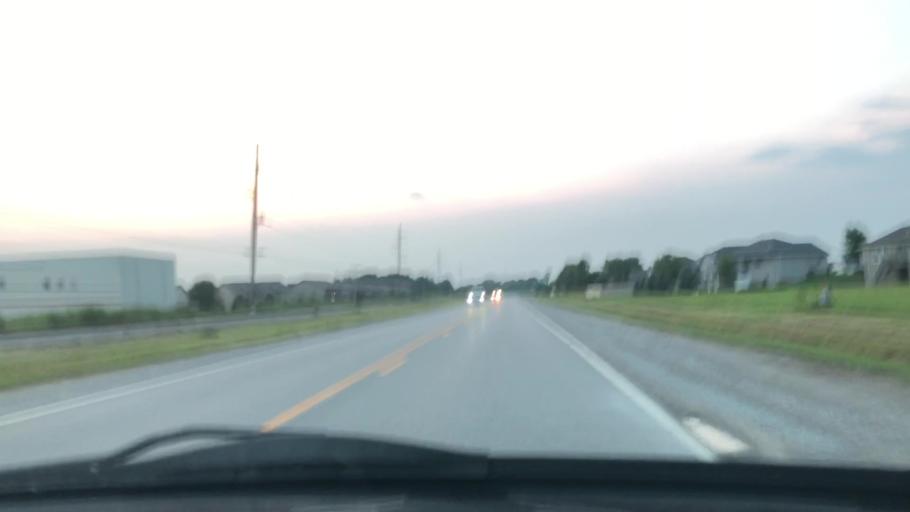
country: US
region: Iowa
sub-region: Johnson County
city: North Liberty
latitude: 41.7625
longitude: -91.6126
